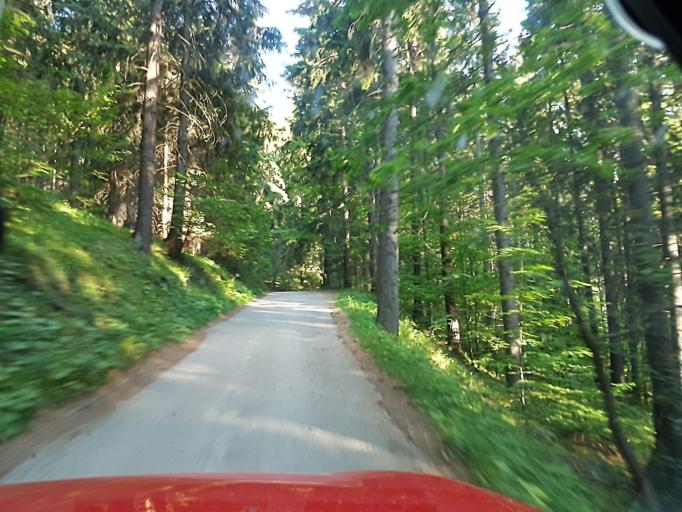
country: SK
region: Zilinsky
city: Ruzomberok
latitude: 49.0620
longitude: 19.2750
